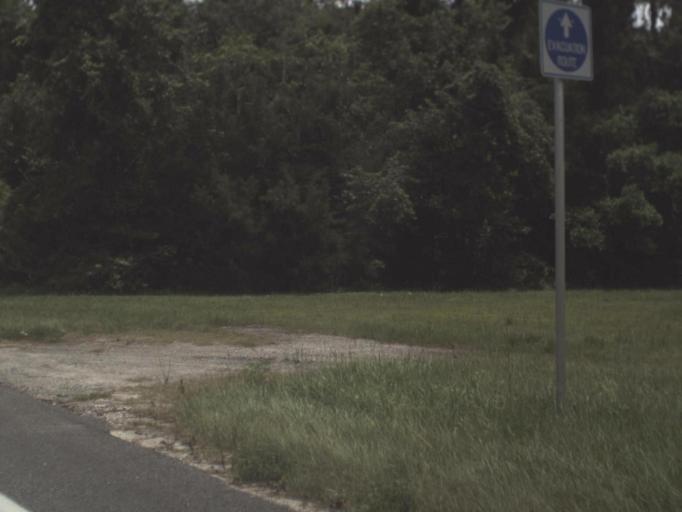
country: US
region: Florida
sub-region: Taylor County
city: Perry
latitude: 30.1048
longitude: -83.6080
